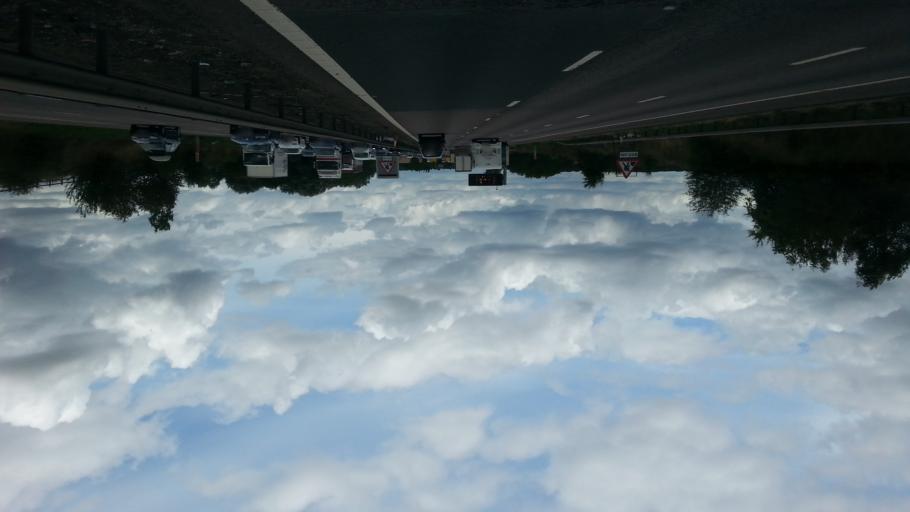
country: GB
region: England
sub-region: Essex
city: Epping
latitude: 51.7260
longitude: 0.1409
